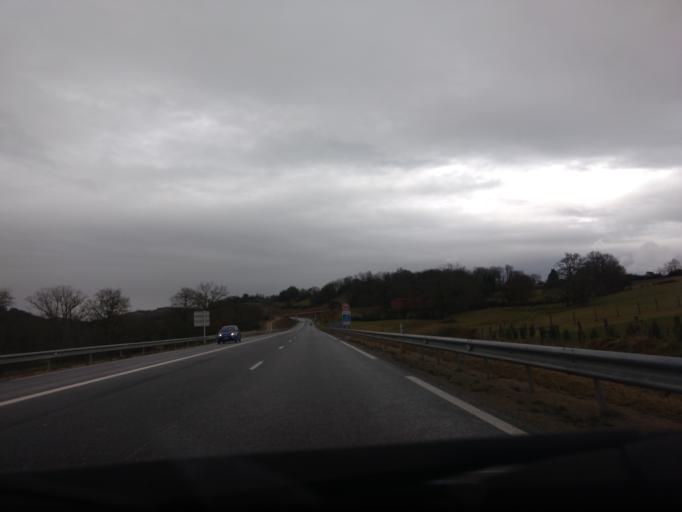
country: FR
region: Midi-Pyrenees
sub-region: Departement de l'Aveyron
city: Firmi
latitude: 44.5205
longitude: 2.3400
